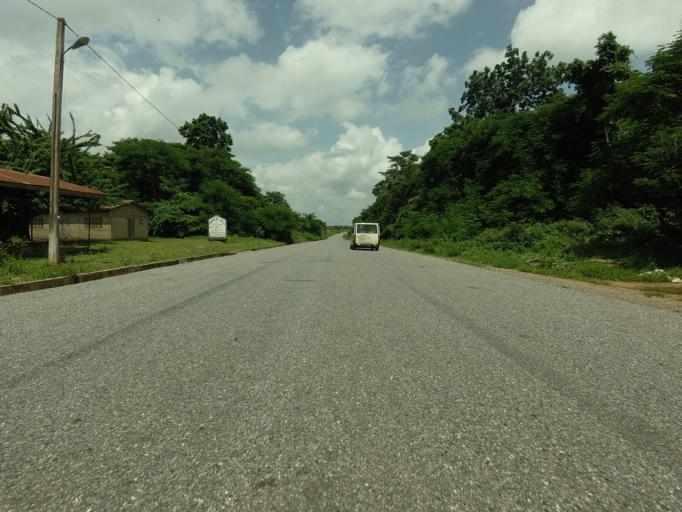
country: GH
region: Volta
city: Kpandu
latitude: 6.8465
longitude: 0.3915
